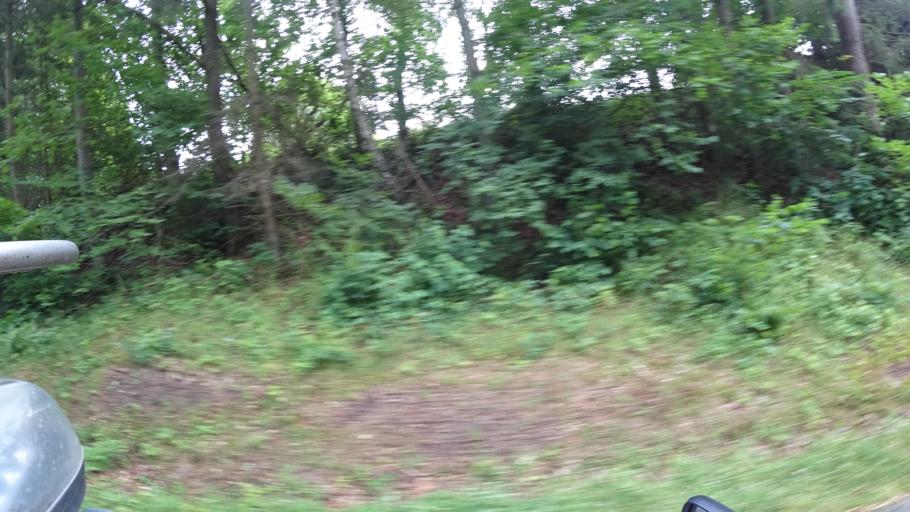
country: SE
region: Skane
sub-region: Kristianstads Kommun
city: Degeberga
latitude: 55.7154
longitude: 13.9869
